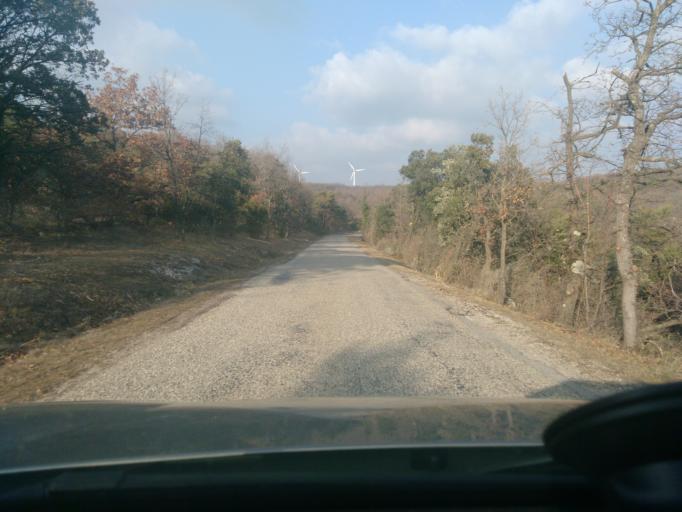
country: FR
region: Rhone-Alpes
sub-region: Departement de la Drome
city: Grignan
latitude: 44.4792
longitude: 4.8737
